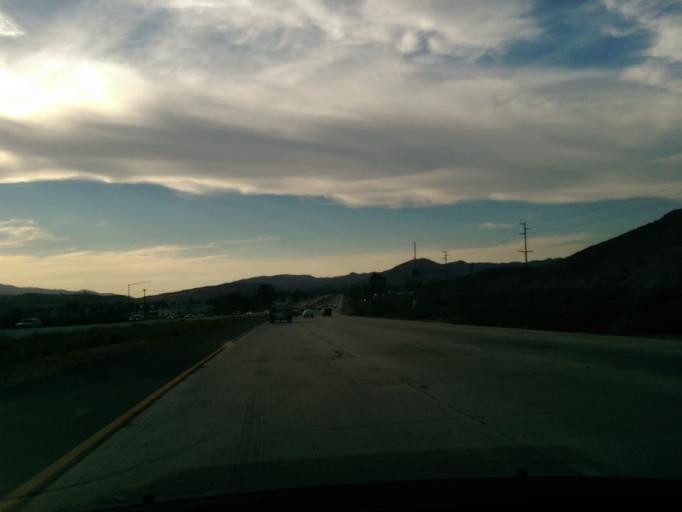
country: US
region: California
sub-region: Riverside County
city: Lake Elsinore
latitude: 33.6781
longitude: -117.3245
